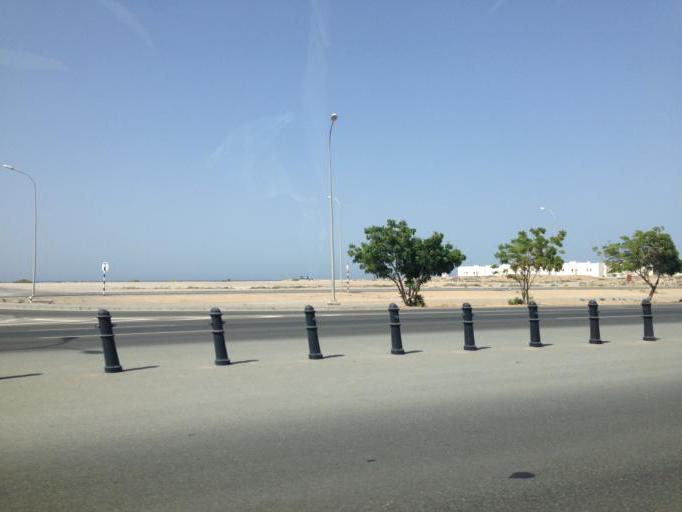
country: OM
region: Muhafazat Masqat
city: Bawshar
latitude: 23.6049
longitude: 58.3252
